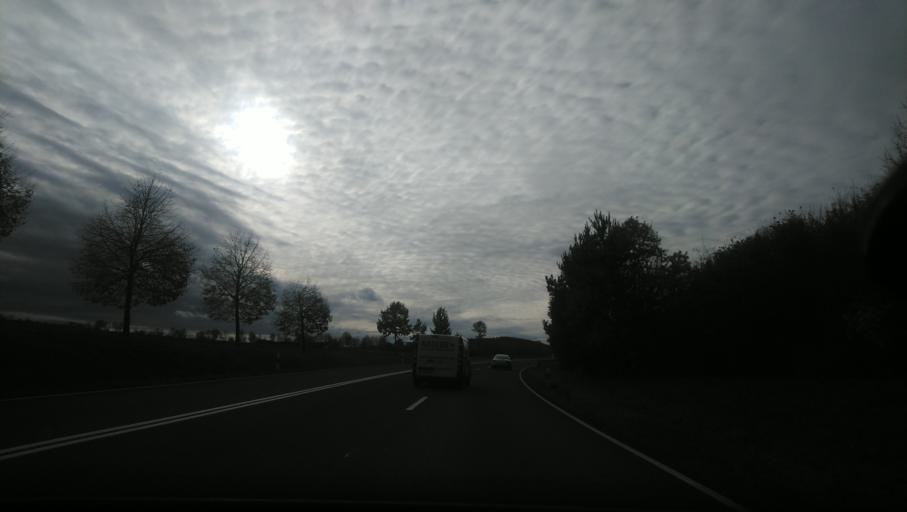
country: DE
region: Saxony
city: Zwonitz
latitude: 50.6376
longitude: 12.8209
